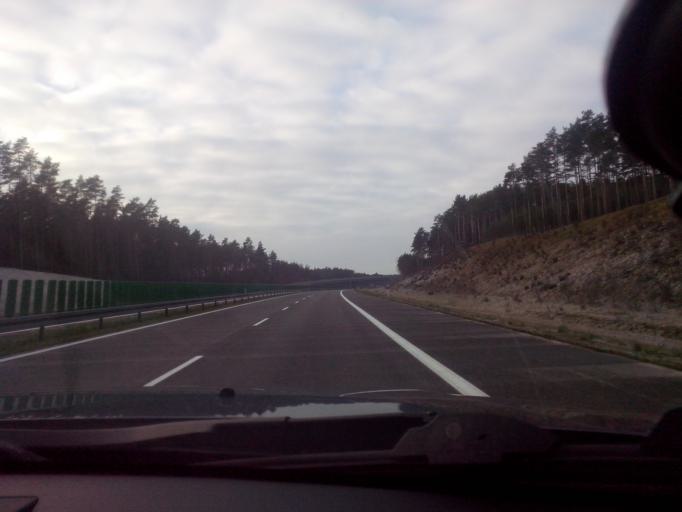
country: PL
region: Lubusz
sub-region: Powiat sulecinski
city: Torzym
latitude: 52.3248
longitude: 15.0629
